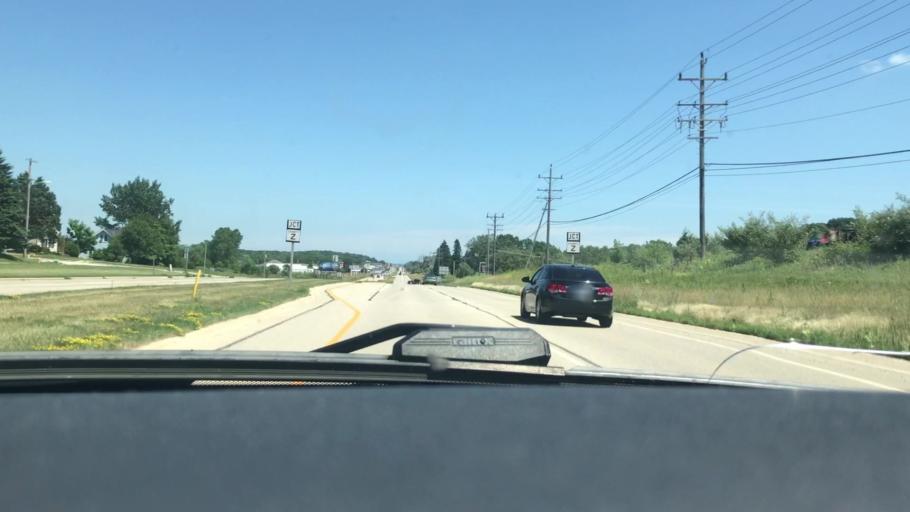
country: US
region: Wisconsin
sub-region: Washington County
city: West Bend
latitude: 43.4274
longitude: -88.2445
